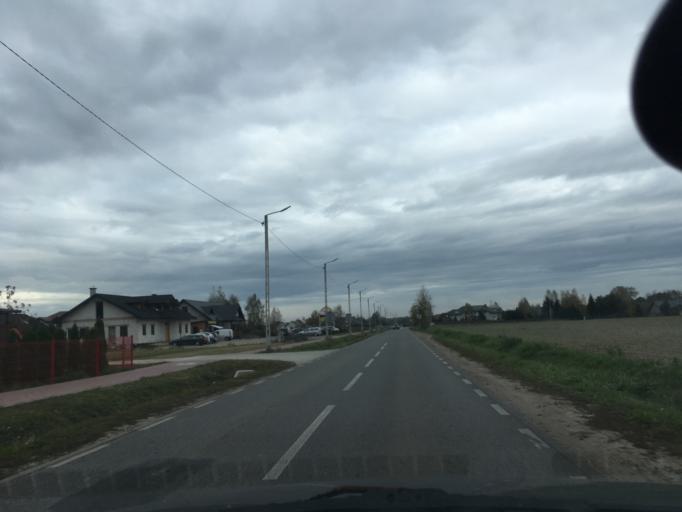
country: PL
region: Lodz Voivodeship
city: Zabia Wola
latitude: 52.0181
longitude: 20.7310
